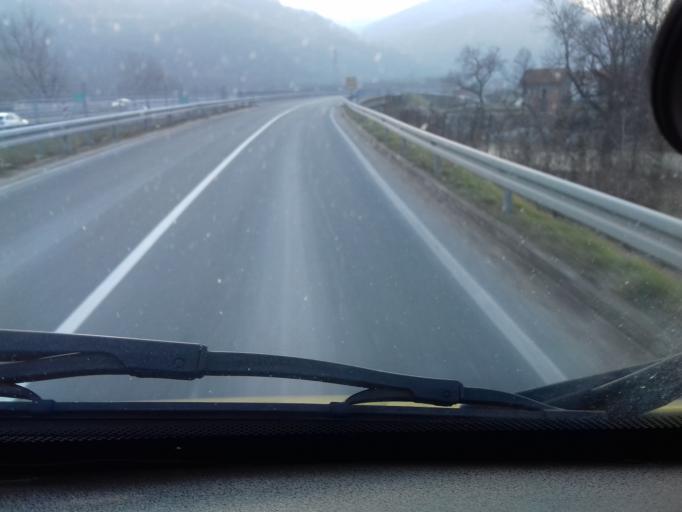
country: BA
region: Federation of Bosnia and Herzegovina
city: Kakanj
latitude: 44.1321
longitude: 18.0682
